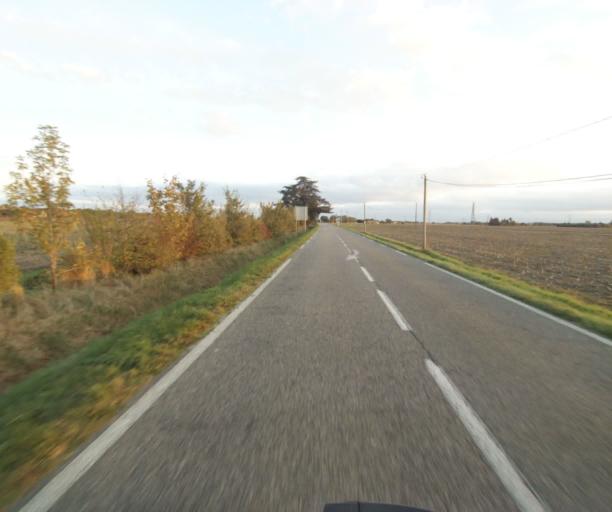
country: FR
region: Midi-Pyrenees
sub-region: Departement du Tarn-et-Garonne
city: Verdun-sur-Garonne
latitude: 43.8211
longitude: 1.2453
